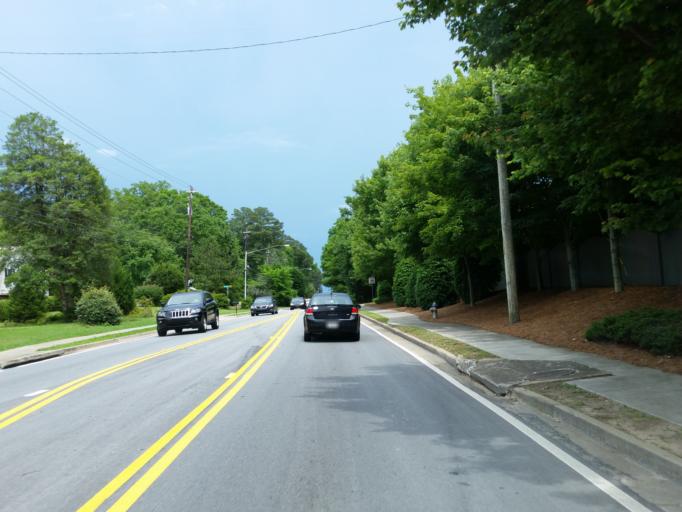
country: US
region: Georgia
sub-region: Fulton County
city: Alpharetta
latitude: 34.0728
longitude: -84.3177
